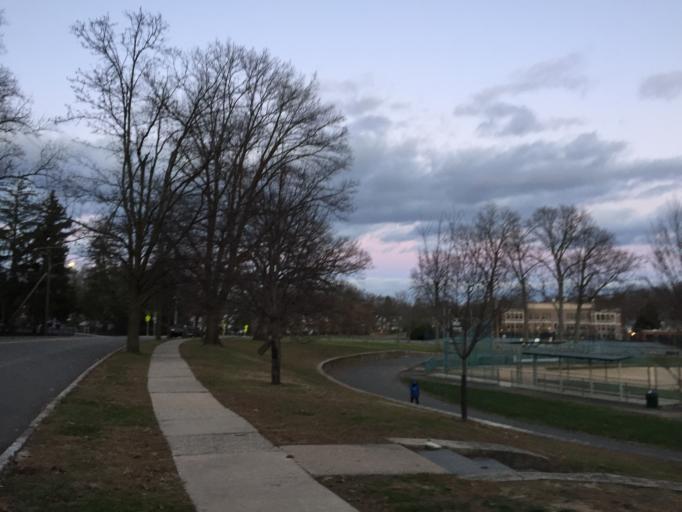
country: US
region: New Jersey
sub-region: Union County
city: Summit
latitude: 40.7088
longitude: -74.3674
